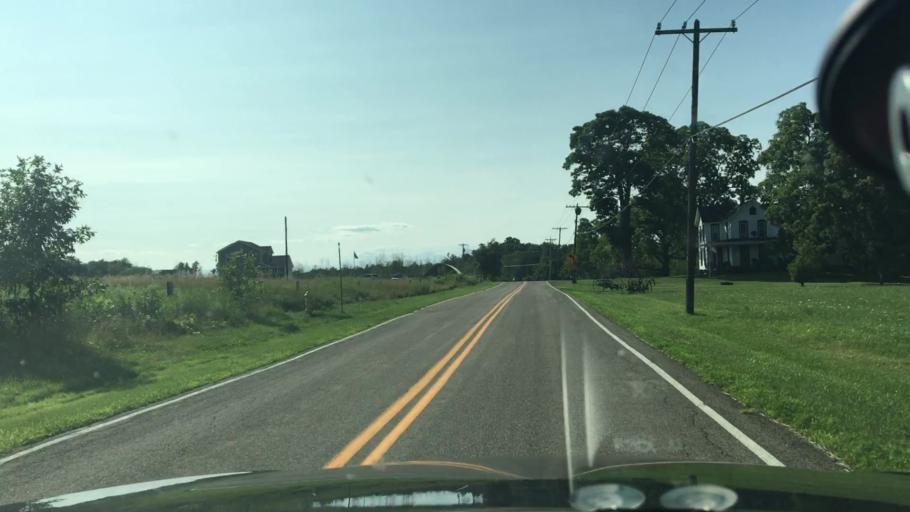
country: US
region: New York
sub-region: Erie County
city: North Collins
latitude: 42.6283
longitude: -78.9778
